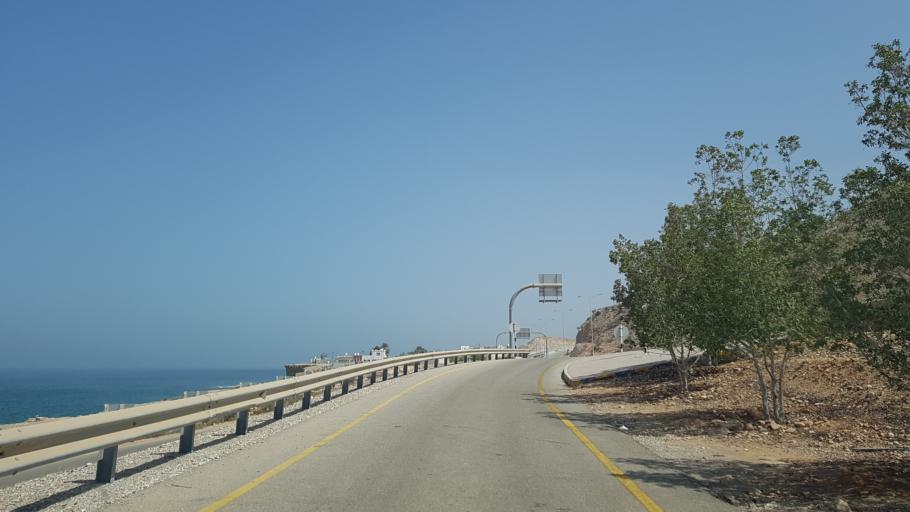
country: OM
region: Ash Sharqiyah
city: Sur
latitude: 22.8436
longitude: 59.2421
